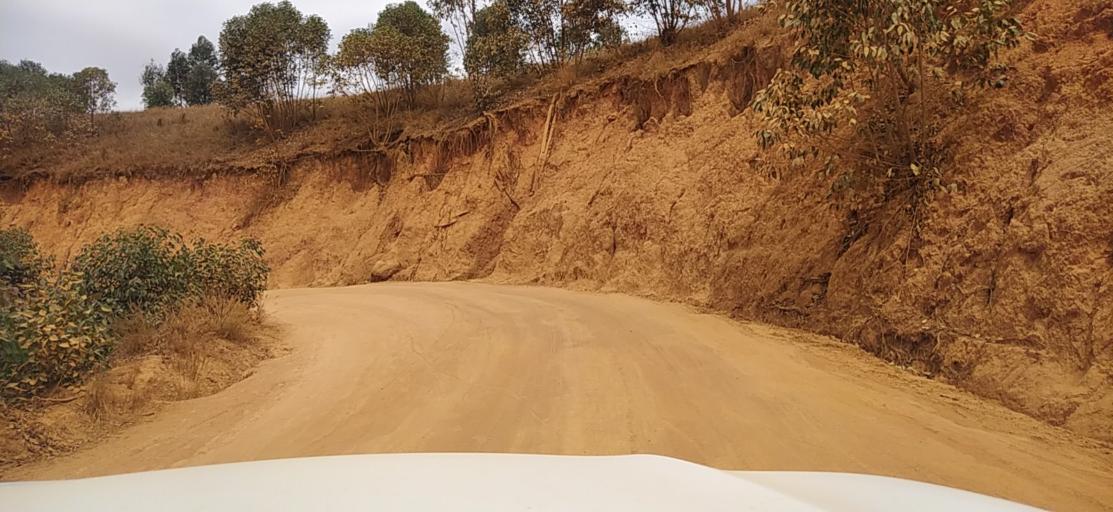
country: MG
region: Alaotra Mangoro
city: Ambatondrazaka
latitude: -17.9977
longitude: 48.2654
